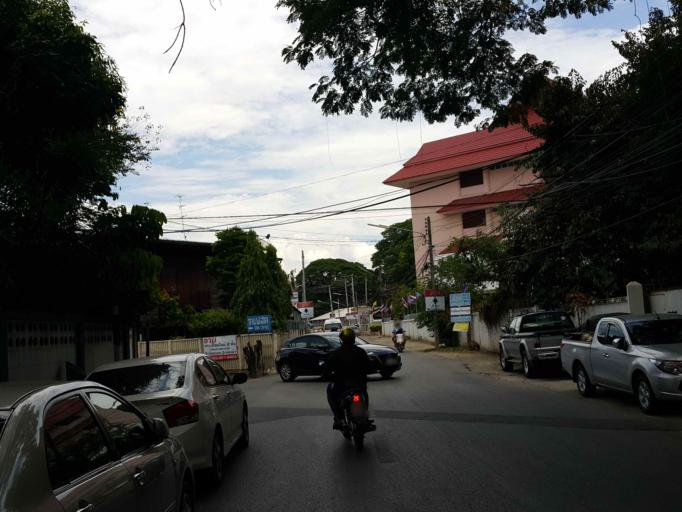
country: TH
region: Chiang Mai
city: Chiang Mai
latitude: 18.7833
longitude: 99.0132
